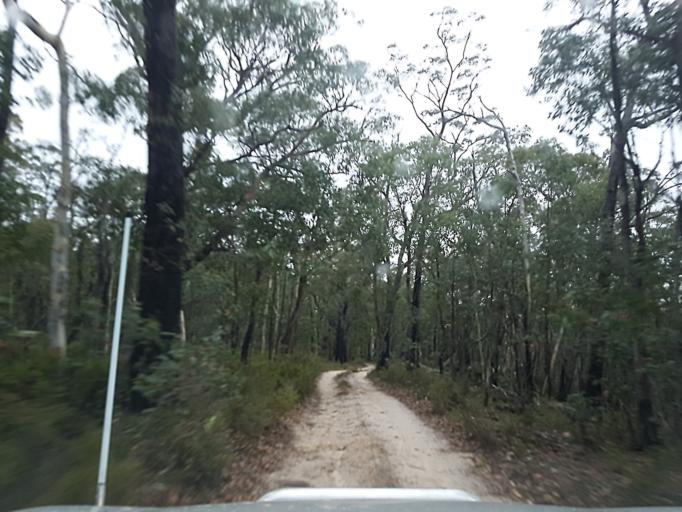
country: AU
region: New South Wales
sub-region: Snowy River
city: Jindabyne
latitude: -36.8500
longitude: 148.2254
